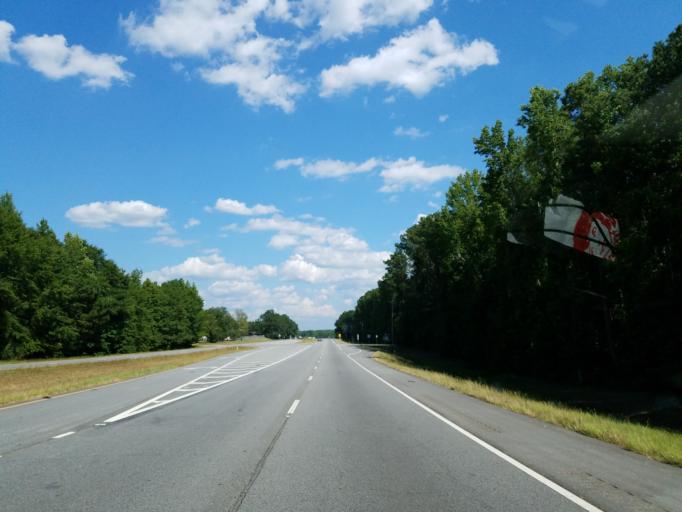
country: US
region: Georgia
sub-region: Lamar County
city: Barnesville
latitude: 33.1060
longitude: -84.1932
